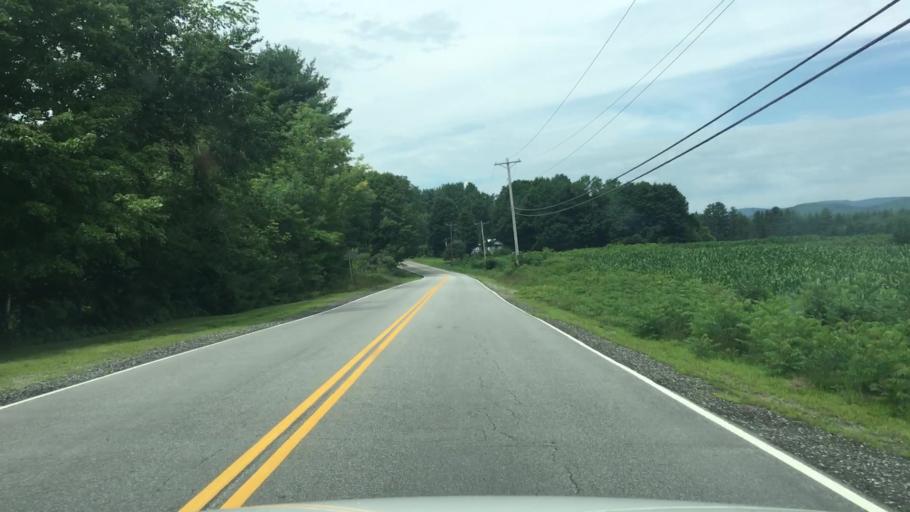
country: US
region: New Hampshire
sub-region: Grafton County
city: Plymouth
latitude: 43.7780
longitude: -71.7447
